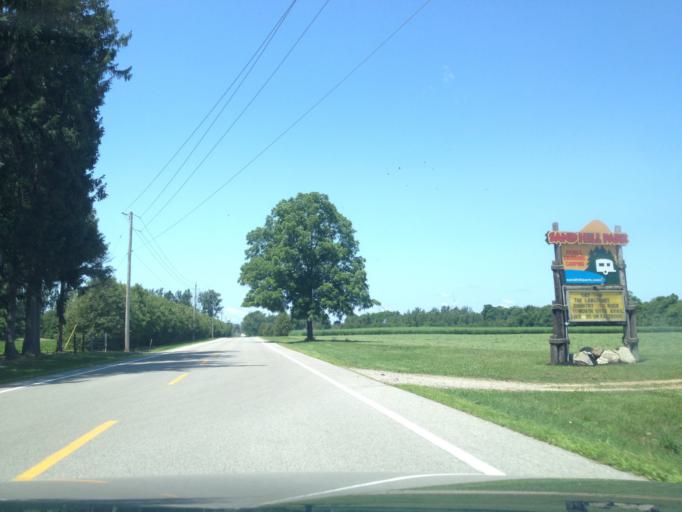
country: CA
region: Ontario
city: Norfolk County
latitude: 42.5940
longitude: -80.6415
